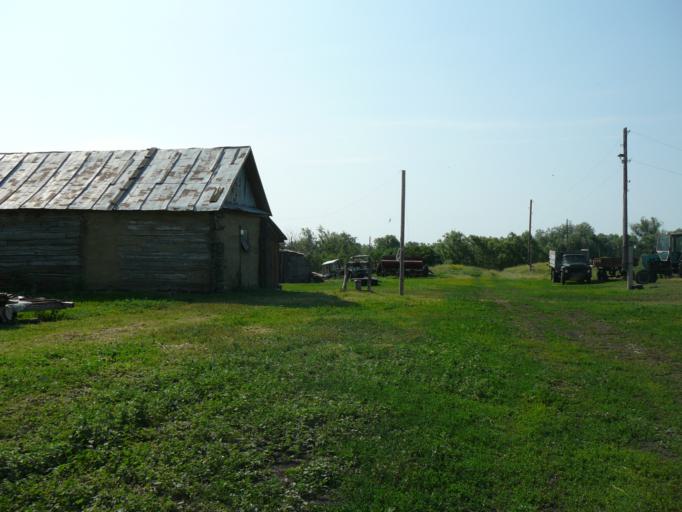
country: RU
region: Penza
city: Tamala
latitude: 52.3458
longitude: 43.2481
